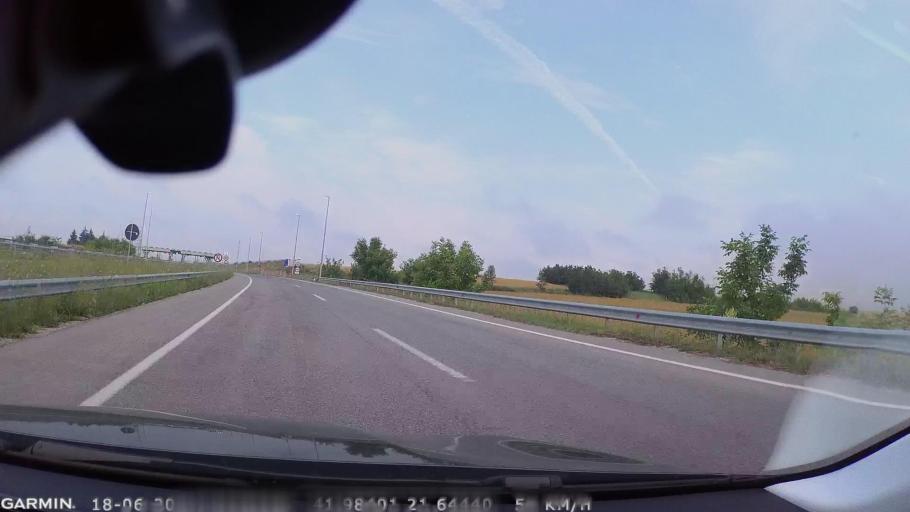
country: MK
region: Petrovec
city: Sredno Konjare
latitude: 41.9548
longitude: 21.7499
